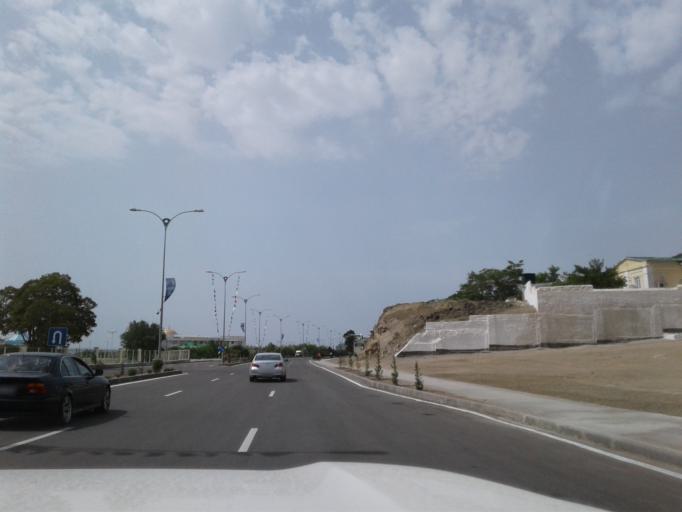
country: TM
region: Balkan
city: Turkmenbasy
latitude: 39.9969
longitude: 52.9919
